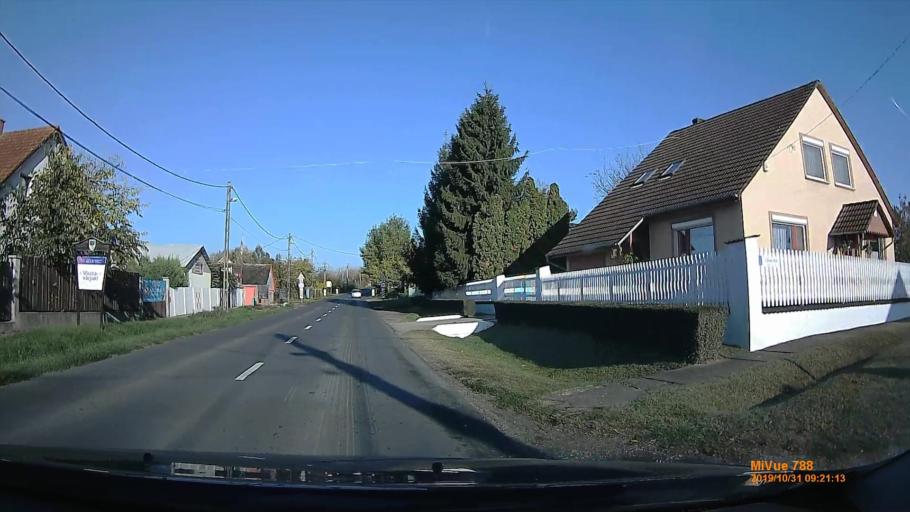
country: HU
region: Pest
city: Gyomro
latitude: 47.4294
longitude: 19.3818
